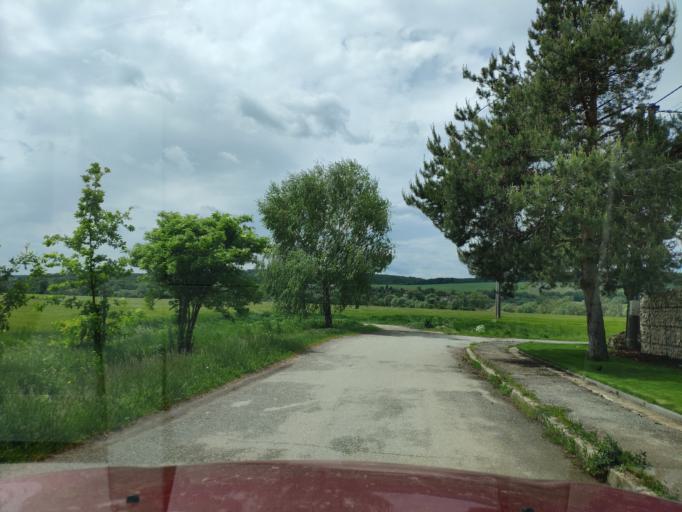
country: SK
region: Kosicky
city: Kosice
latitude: 48.7256
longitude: 21.3403
